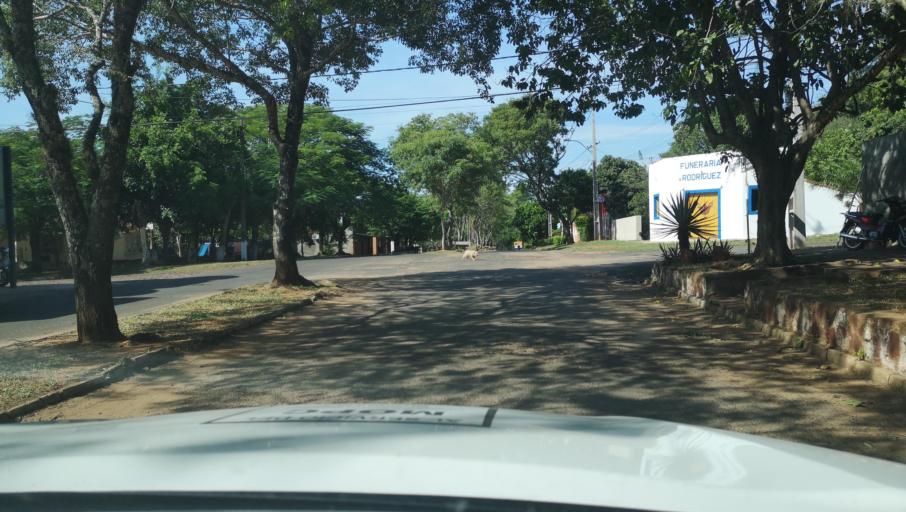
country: PY
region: Misiones
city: Santa Maria
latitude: -26.8916
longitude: -57.0193
